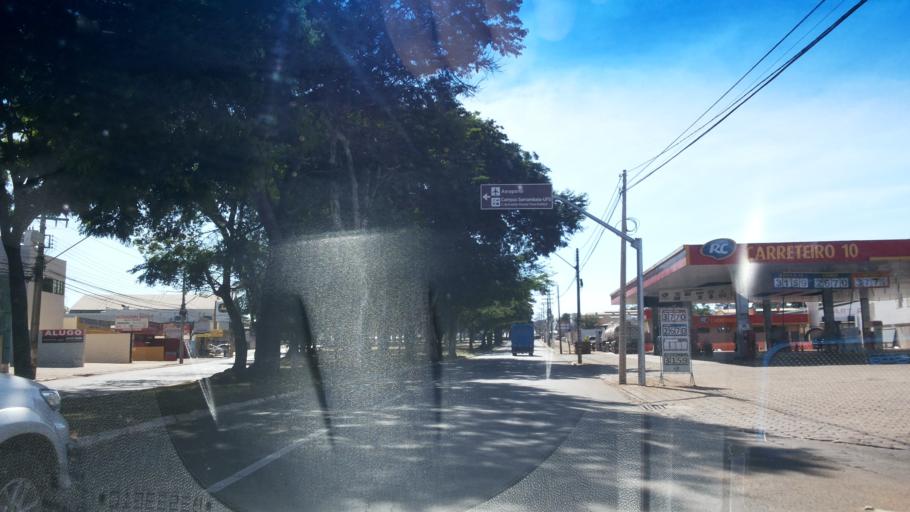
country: BR
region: Goias
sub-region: Goiania
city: Goiania
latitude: -16.6414
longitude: -49.2411
